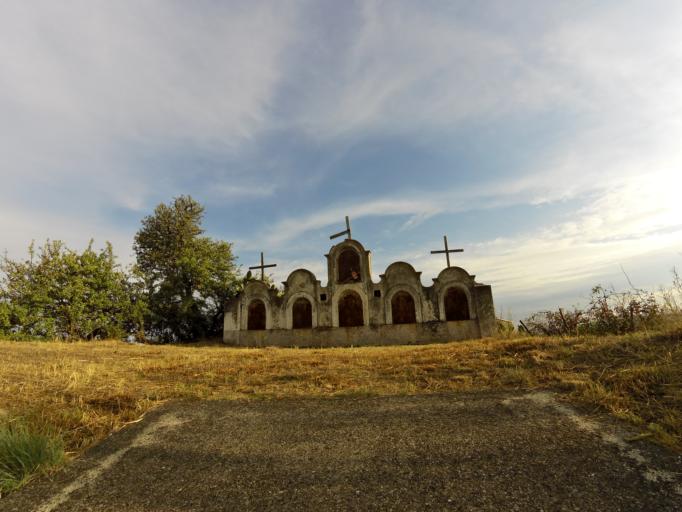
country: IT
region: Calabria
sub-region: Provincia di Reggio Calabria
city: Stignano
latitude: 38.4138
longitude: 16.4705
